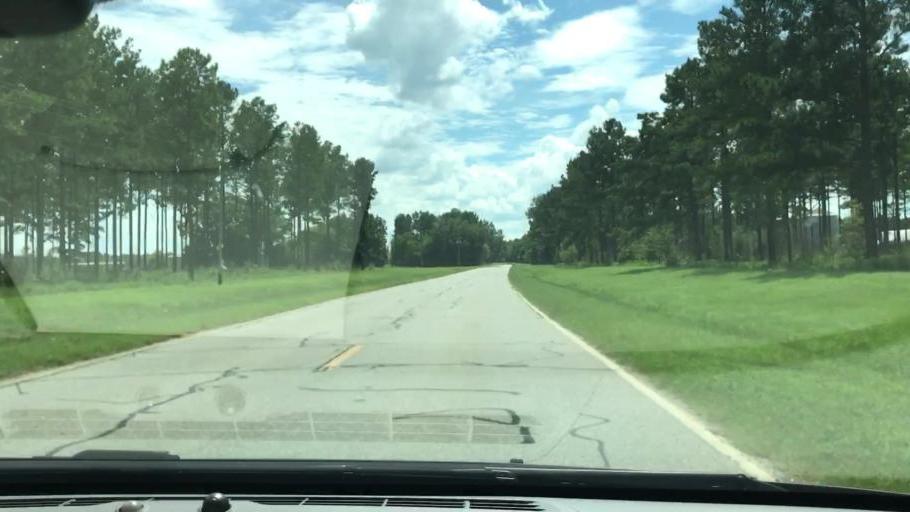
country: US
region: Georgia
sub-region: Quitman County
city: Georgetown
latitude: 32.0521
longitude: -85.0364
